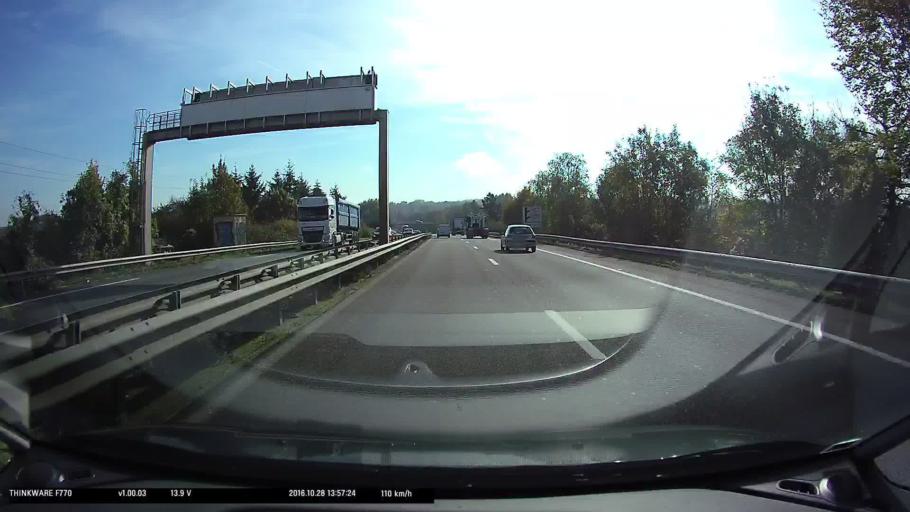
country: FR
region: Lorraine
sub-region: Departement de Meurthe-et-Moselle
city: Villers-les-Nancy
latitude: 48.6595
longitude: 6.1256
